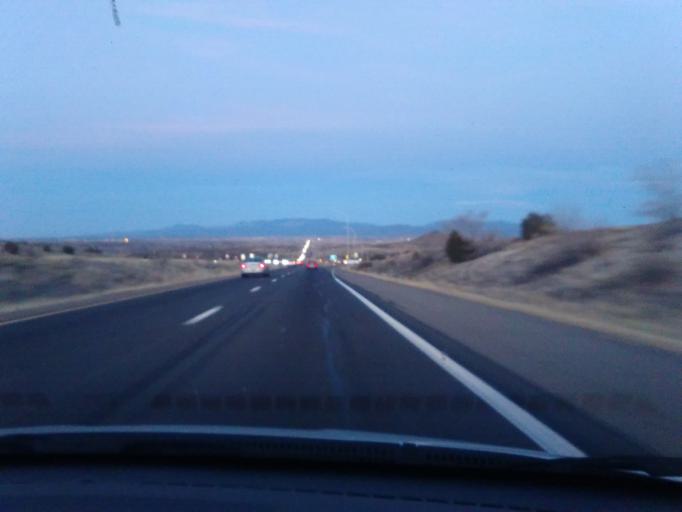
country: US
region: New Mexico
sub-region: Santa Fe County
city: La Cienega
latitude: 35.5250
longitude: -106.1609
